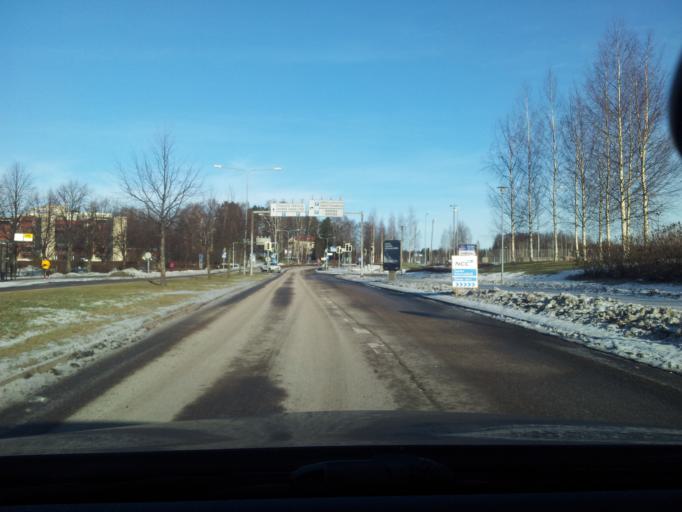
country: FI
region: Uusimaa
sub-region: Helsinki
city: Koukkuniemi
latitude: 60.1776
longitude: 24.7788
